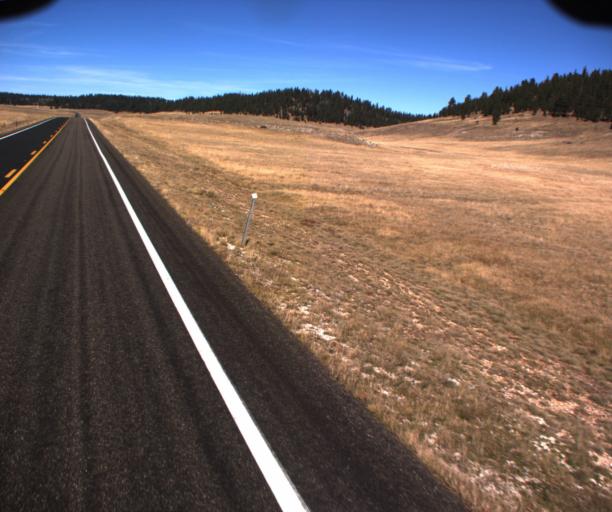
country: US
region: Arizona
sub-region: Coconino County
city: Grand Canyon
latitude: 36.4800
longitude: -112.1269
